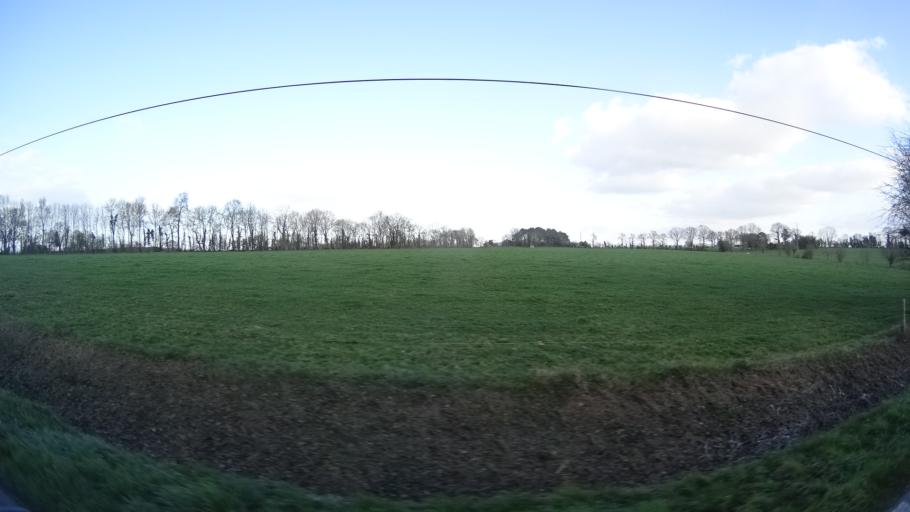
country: FR
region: Pays de la Loire
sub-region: Departement de la Loire-Atlantique
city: Fegreac
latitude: 47.5749
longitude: -1.9826
